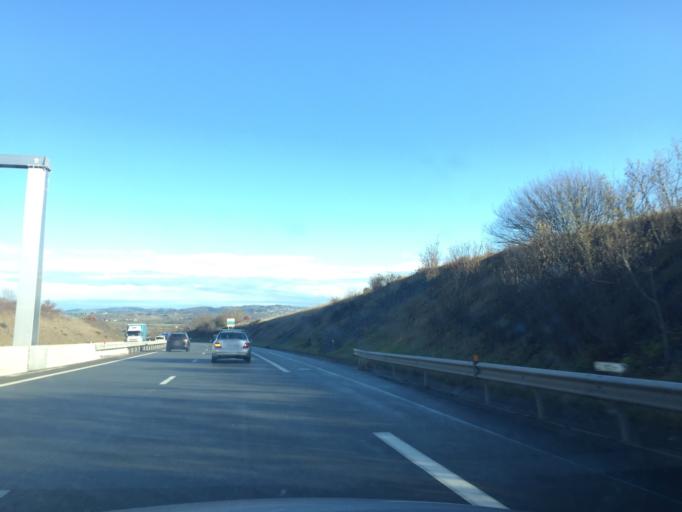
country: FR
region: Rhone-Alpes
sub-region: Departement de la Loire
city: Balbigny
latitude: 45.8253
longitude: 4.1376
